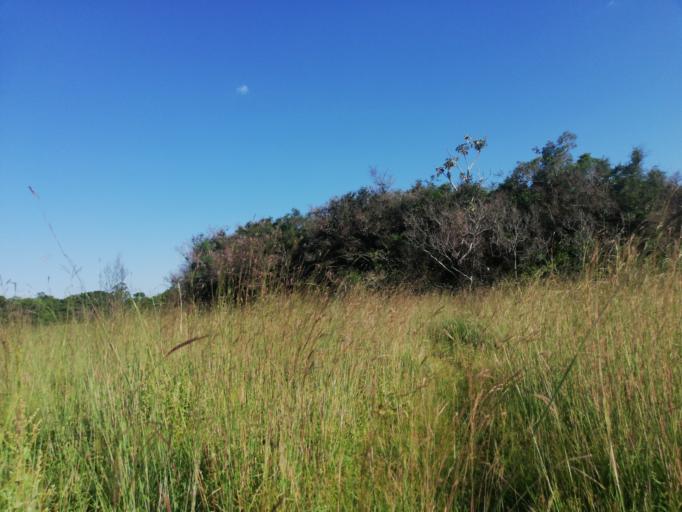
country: AR
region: Corrientes
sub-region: Departamento de San Miguel
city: San Miguel
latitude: -27.9889
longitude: -57.5422
